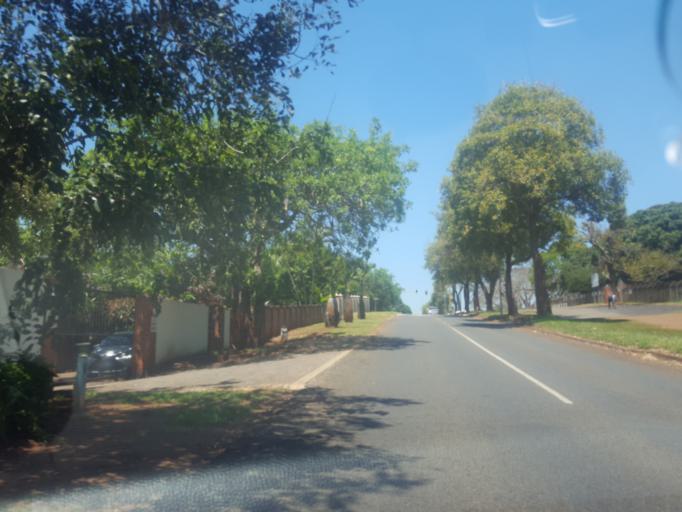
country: ZA
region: KwaZulu-Natal
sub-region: uThungulu District Municipality
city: Empangeni
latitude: -28.7539
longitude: 31.9024
